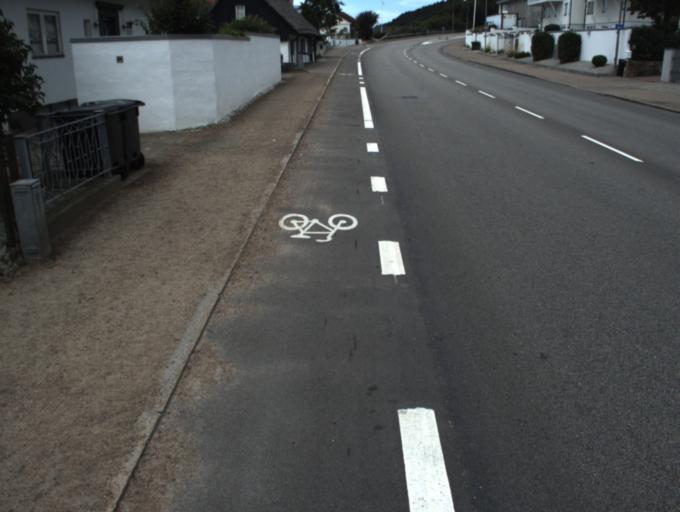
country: SE
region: Skane
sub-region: Helsingborg
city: Helsingborg
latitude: 56.0733
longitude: 12.6678
